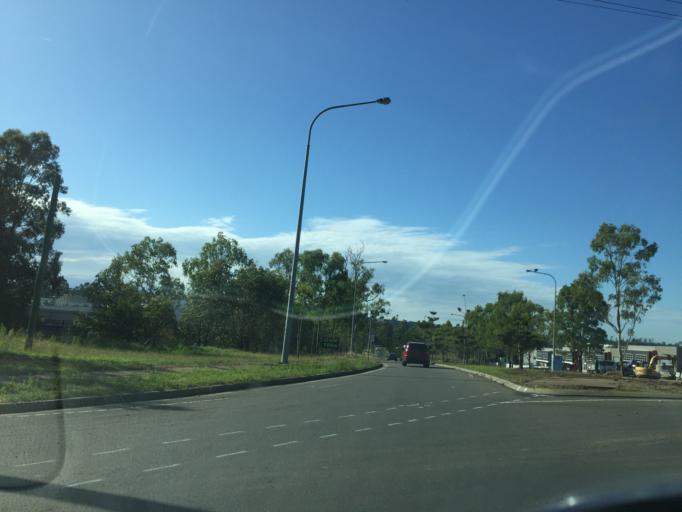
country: AU
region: New South Wales
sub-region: Holroyd
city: Girraween
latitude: -33.8093
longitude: 150.9184
